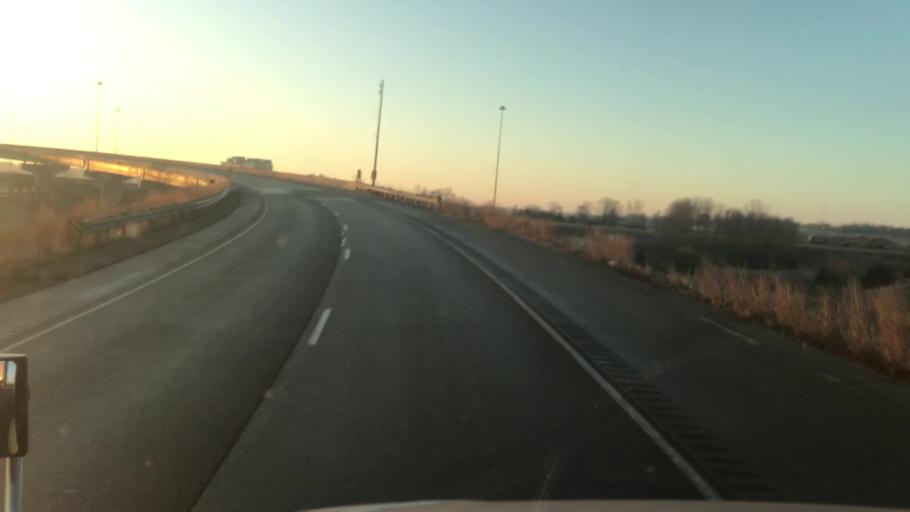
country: US
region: Iowa
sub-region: Black Hawk County
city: Evansdale
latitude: 42.4564
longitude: -92.3146
